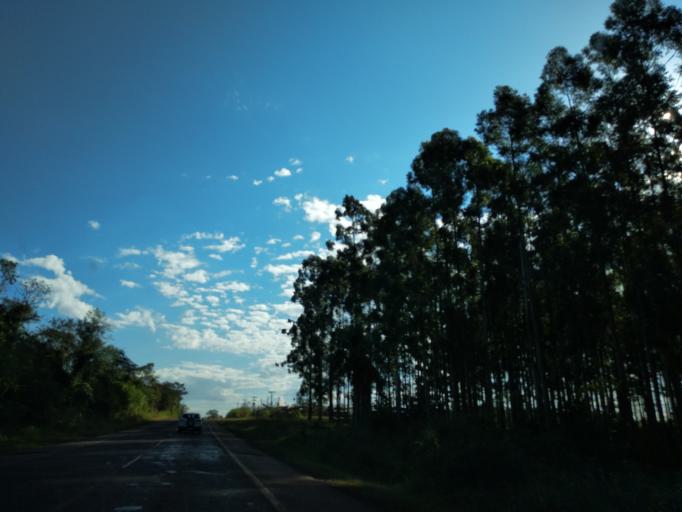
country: AR
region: Misiones
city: Ruiz de Montoya
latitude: -27.0591
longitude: -55.0211
